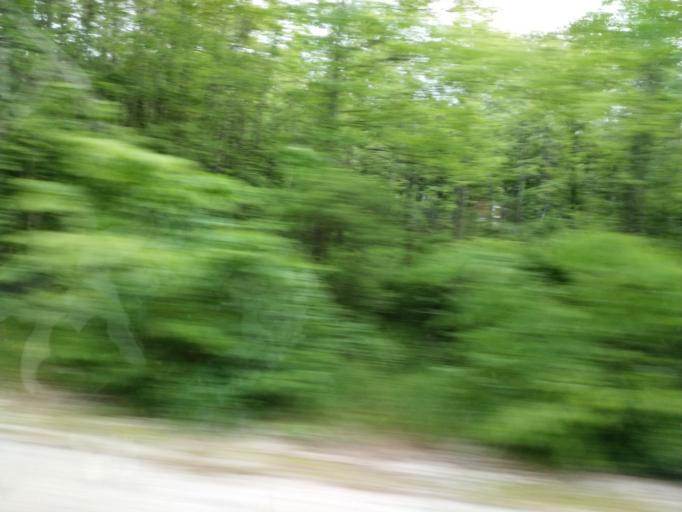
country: US
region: Maine
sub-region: Cumberland County
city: New Gloucester
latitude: 43.8855
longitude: -70.3130
